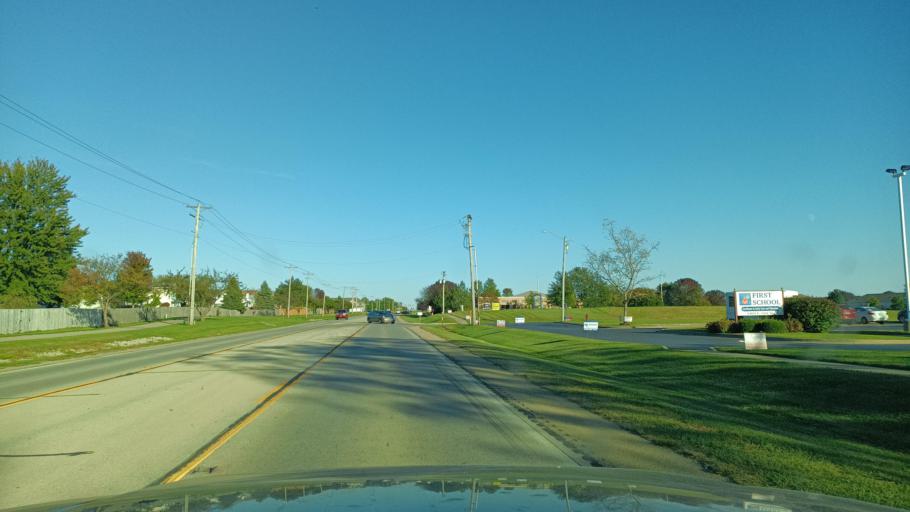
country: US
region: Illinois
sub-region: Champaign County
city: Mahomet
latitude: 40.1873
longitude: -88.3858
